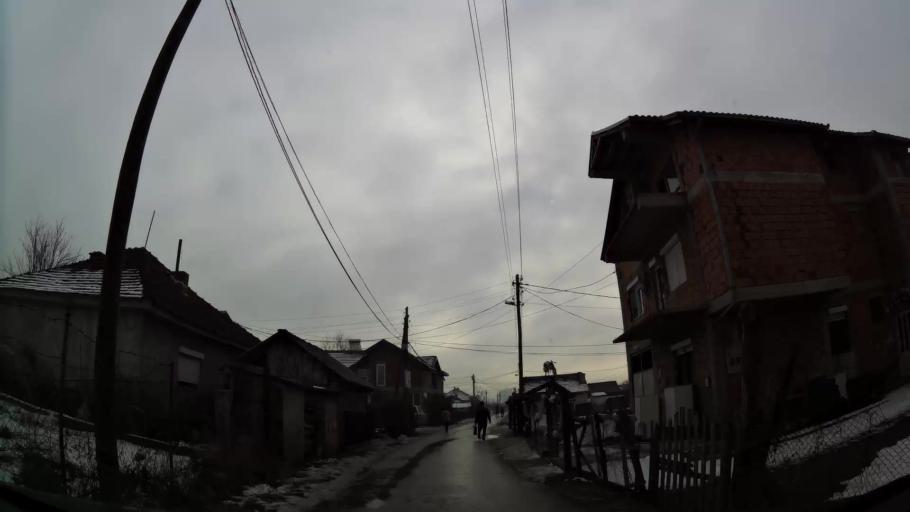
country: MK
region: Ilinden
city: Ilinden
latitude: 41.9939
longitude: 21.5720
